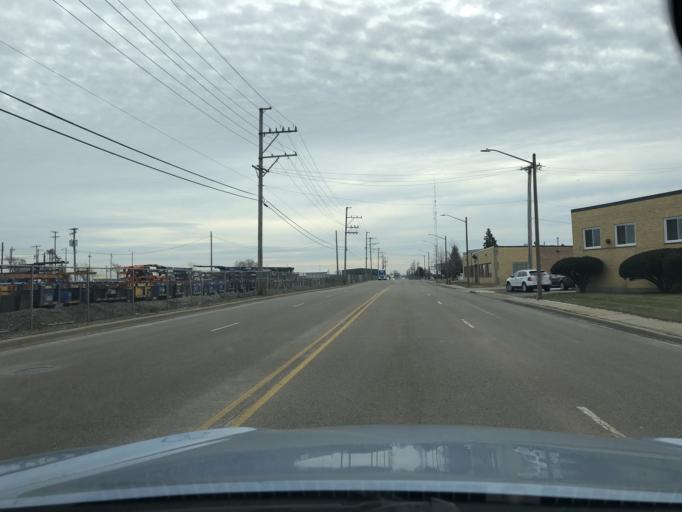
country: US
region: Illinois
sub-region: DuPage County
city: Bensenville
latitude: 41.9530
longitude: -87.9323
